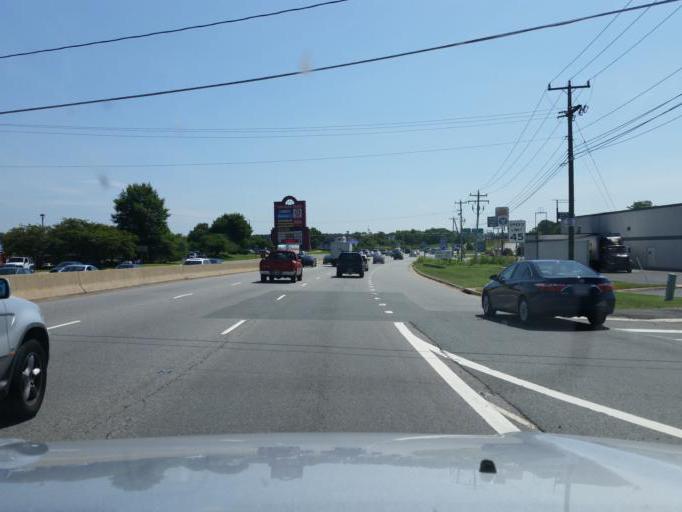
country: US
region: Virginia
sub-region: Stafford County
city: Falmouth
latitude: 38.2953
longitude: -77.5151
